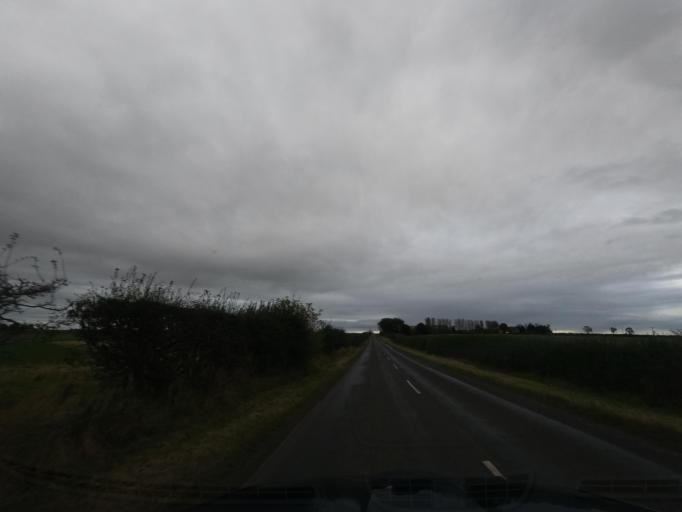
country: GB
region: England
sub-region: Northumberland
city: Ancroft
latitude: 55.7017
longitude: -2.0648
